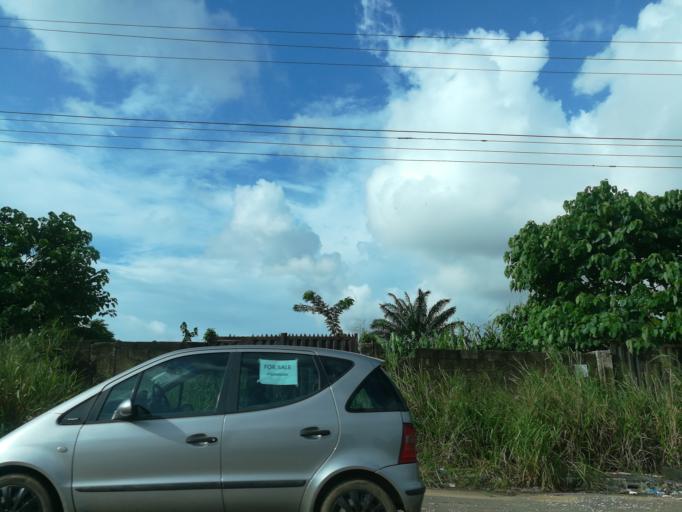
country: NG
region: Lagos
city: Ebute Ikorodu
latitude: 6.5972
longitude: 3.5007
